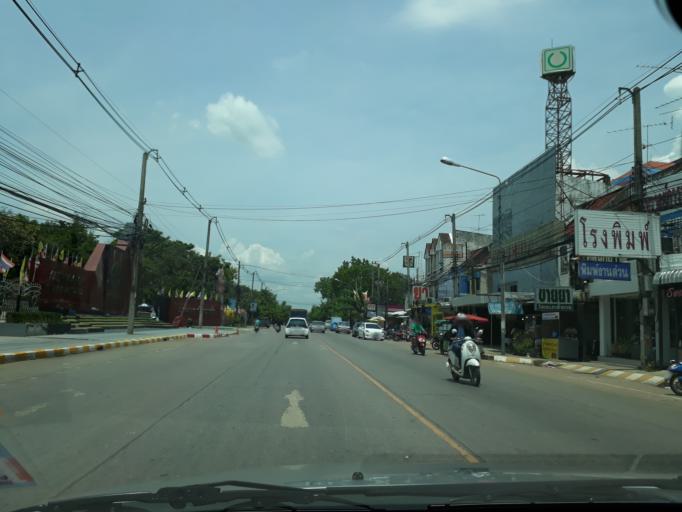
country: TH
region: Khon Kaen
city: Khon Kaen
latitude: 16.4152
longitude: 102.8240
